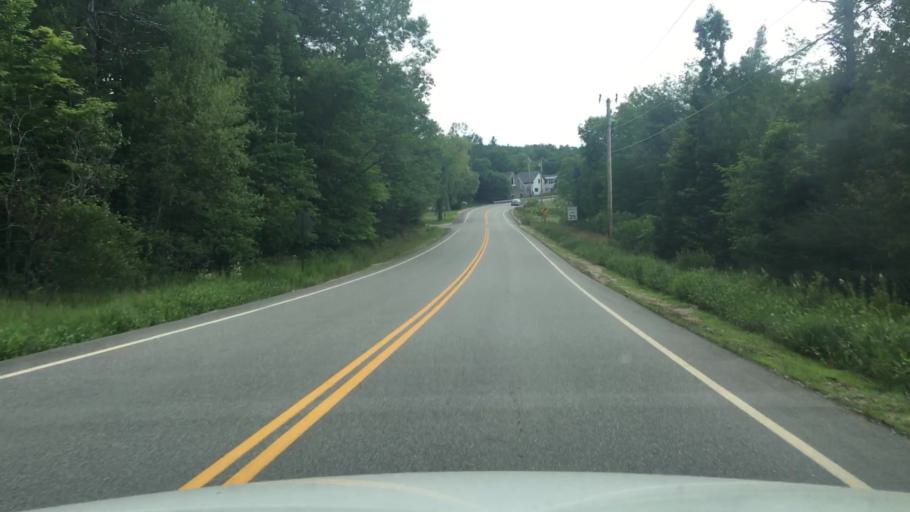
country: US
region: Maine
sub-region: Oxford County
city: Hartford
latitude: 44.3653
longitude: -70.4543
